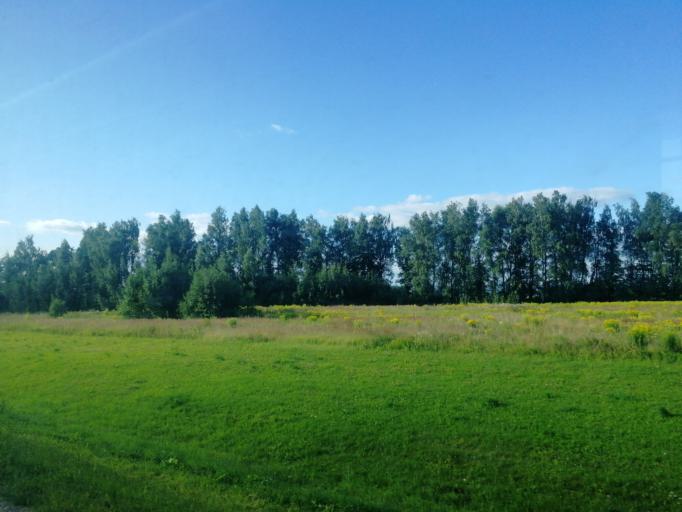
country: RU
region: Tula
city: Leninskiy
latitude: 54.2375
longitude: 37.3477
